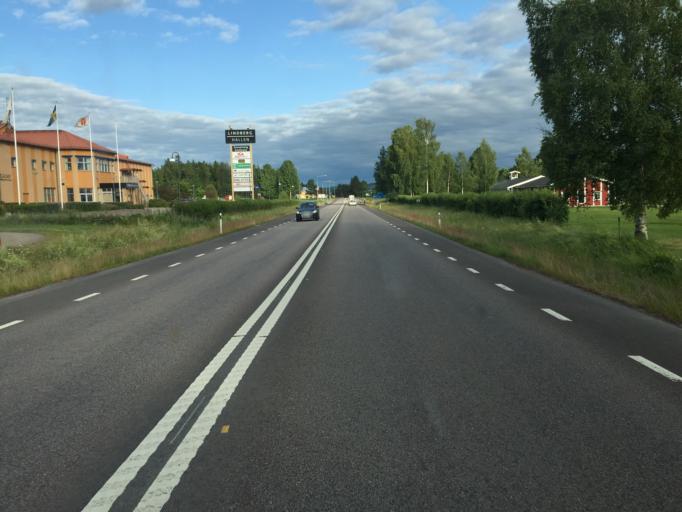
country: SE
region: Dalarna
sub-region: Gagnefs Kommun
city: Djuras
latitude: 60.5599
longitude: 15.1350
